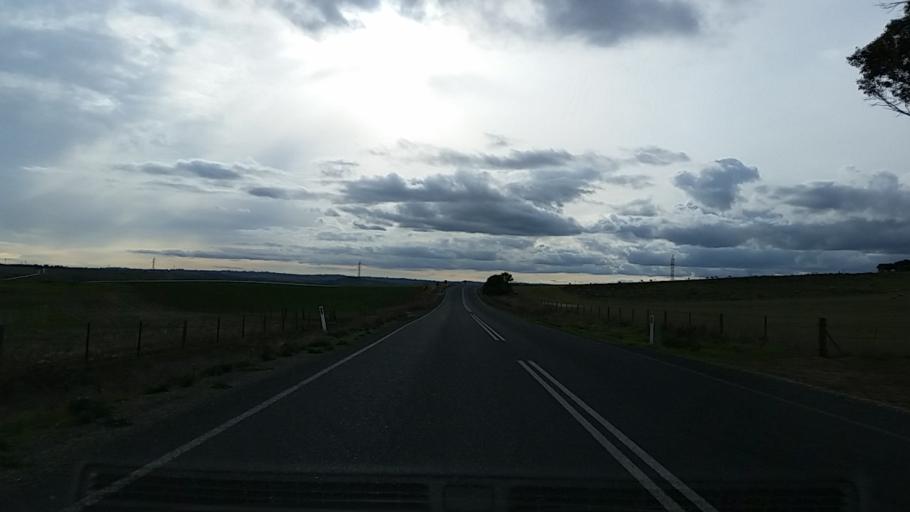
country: AU
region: South Australia
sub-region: Mount Barker
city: Callington
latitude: -35.0691
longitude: 139.0463
